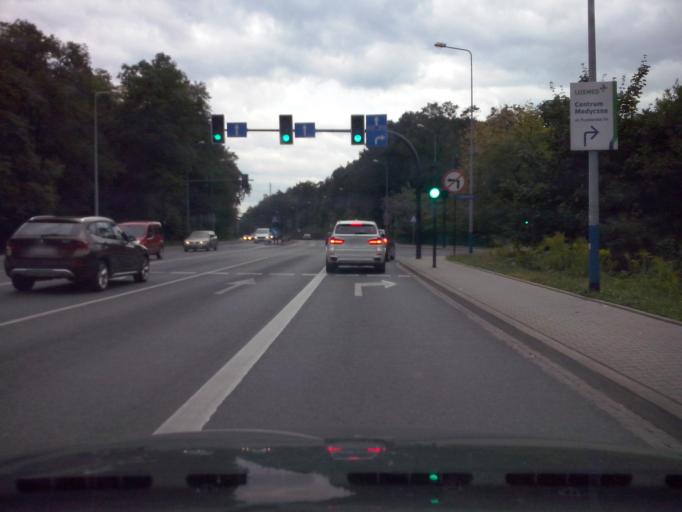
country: PL
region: Lesser Poland Voivodeship
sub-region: Krakow
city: Krakow
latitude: 50.0320
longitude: 19.9480
